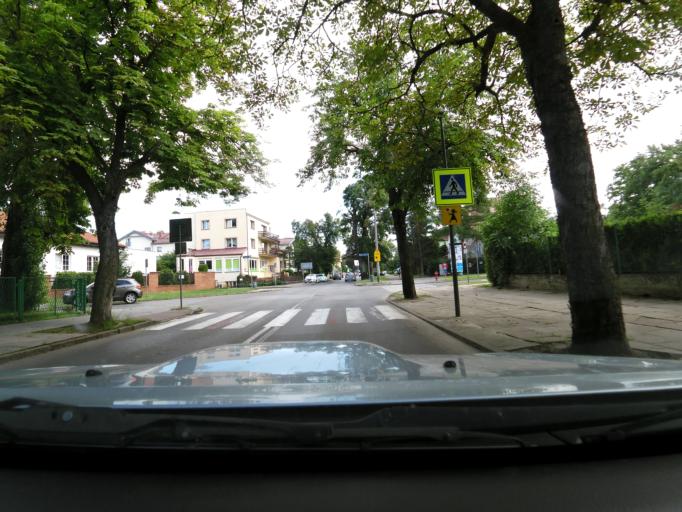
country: PL
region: Pomeranian Voivodeship
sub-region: Sopot
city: Sopot
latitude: 54.4347
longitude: 18.5699
